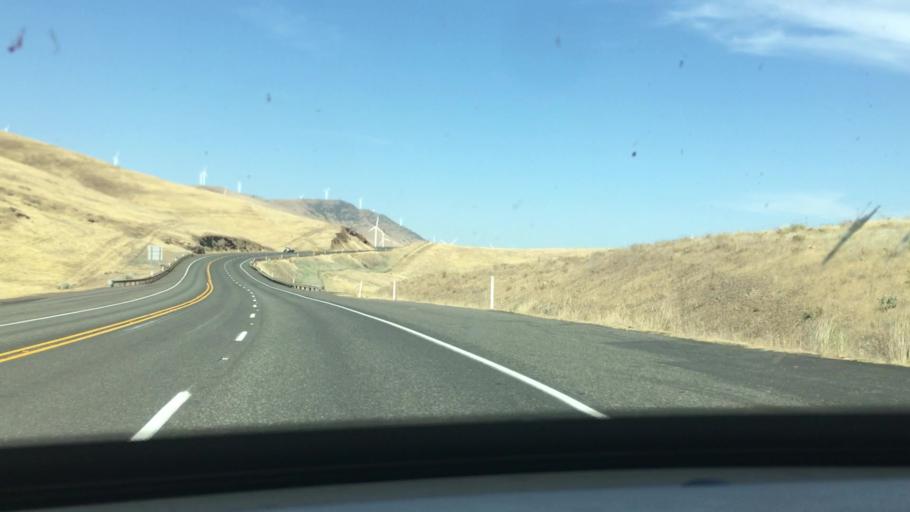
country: US
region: Washington
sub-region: Klickitat County
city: Goldendale
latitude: 45.7065
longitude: -120.8102
